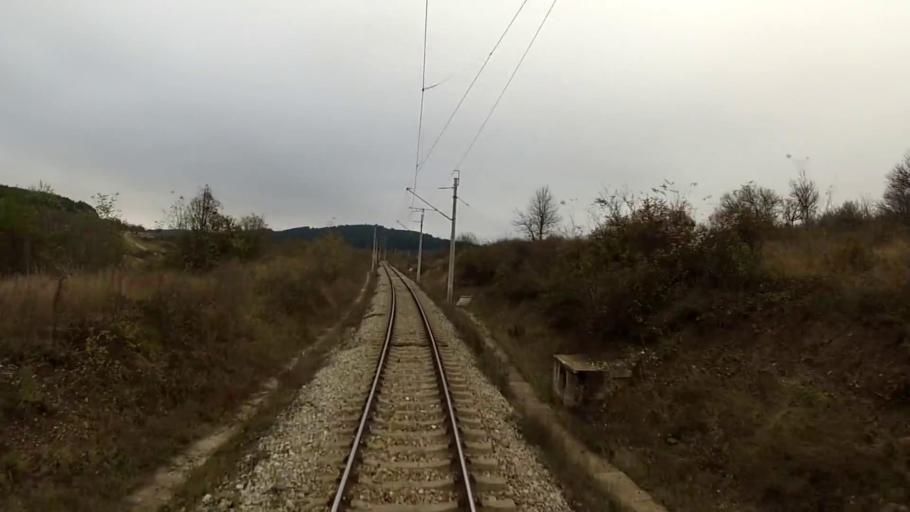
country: BG
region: Sofiya
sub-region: Obshtina Dragoman
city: Dragoman
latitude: 42.9402
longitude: 22.9013
